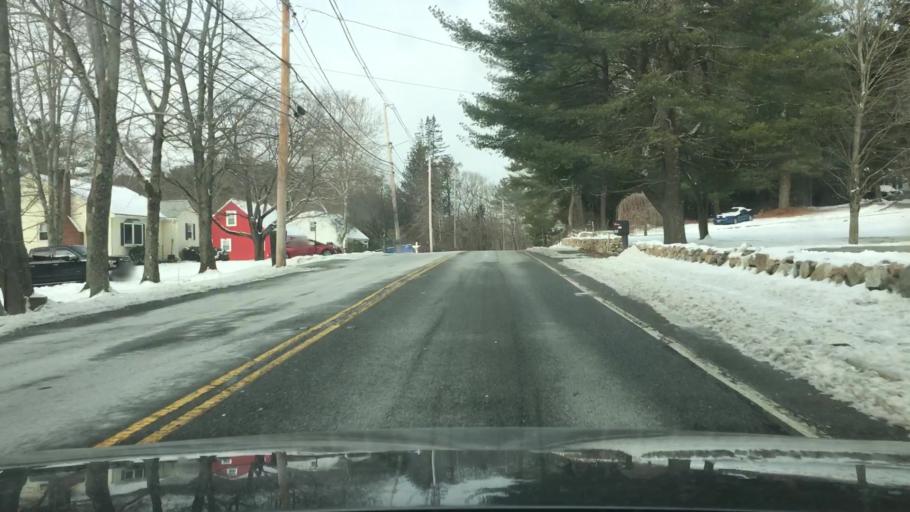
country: US
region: Massachusetts
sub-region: Middlesex County
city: North Reading
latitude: 42.5729
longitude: -71.0513
